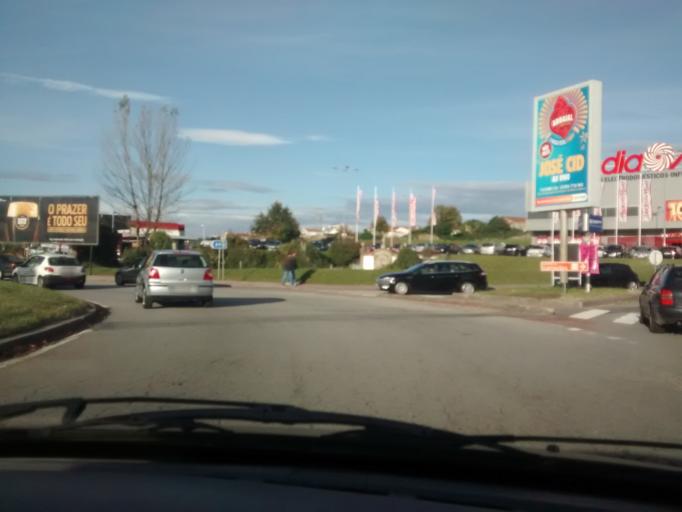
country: PT
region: Braga
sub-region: Braga
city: Braga
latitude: 41.5420
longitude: -8.3987
